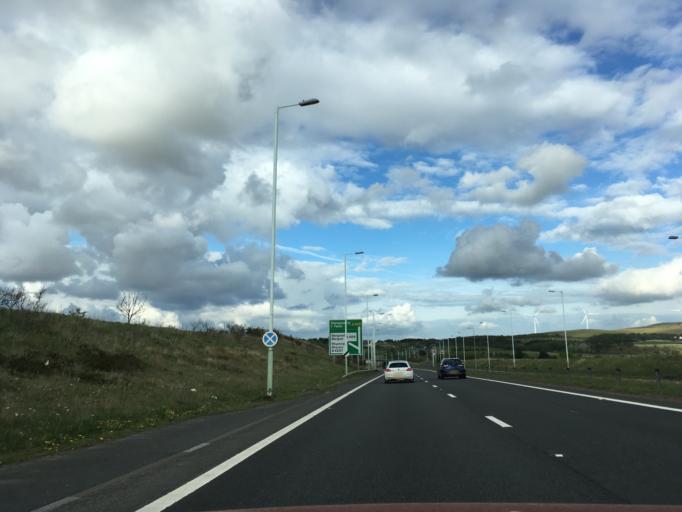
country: GB
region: Wales
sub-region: Caerphilly County Borough
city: Rhymney
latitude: 51.7749
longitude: -3.3085
